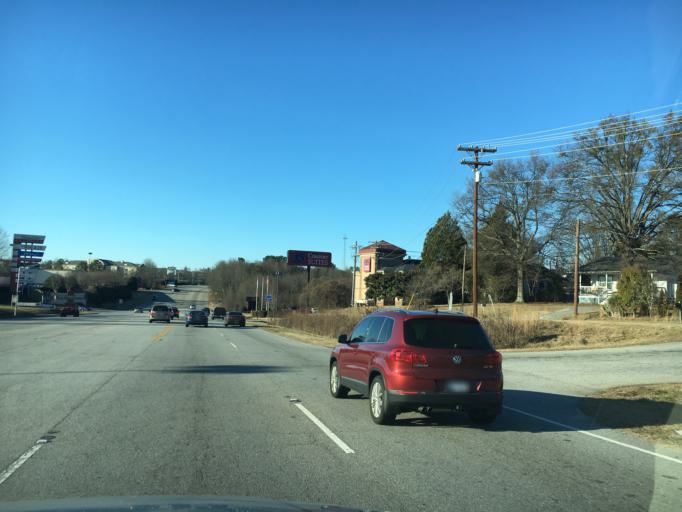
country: US
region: South Carolina
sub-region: Spartanburg County
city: Arcadia
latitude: 34.9430
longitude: -81.9927
